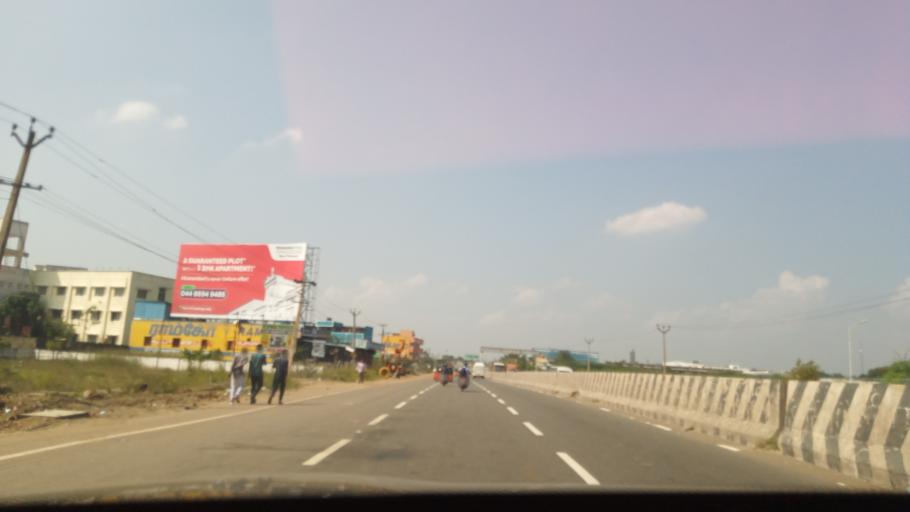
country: IN
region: Tamil Nadu
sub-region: Kancheepuram
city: Madambakkam
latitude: 12.8688
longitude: 79.9740
